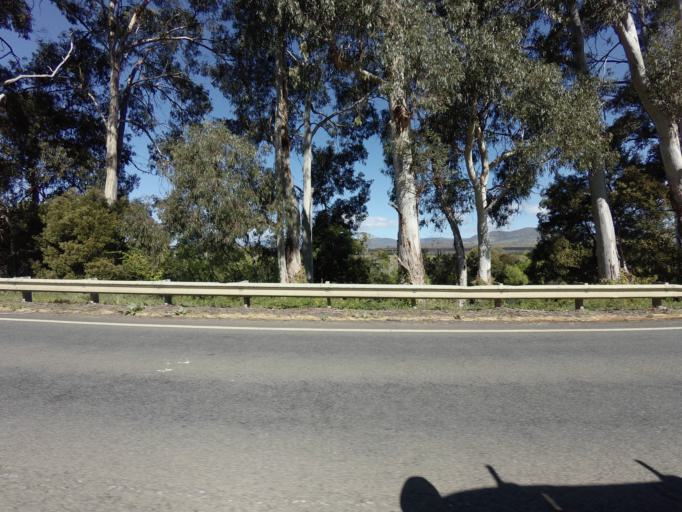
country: AU
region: Tasmania
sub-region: Derwent Valley
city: New Norfolk
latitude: -42.7340
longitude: 146.9652
